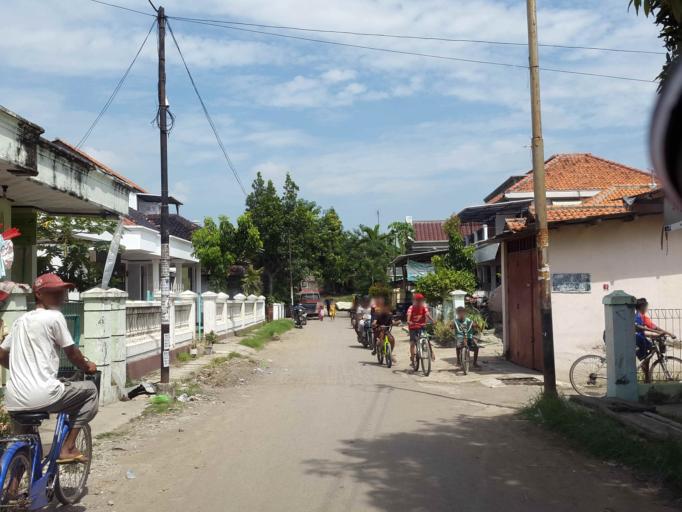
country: ID
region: Central Java
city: Dukuhturi
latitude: -6.8656
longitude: 109.0360
